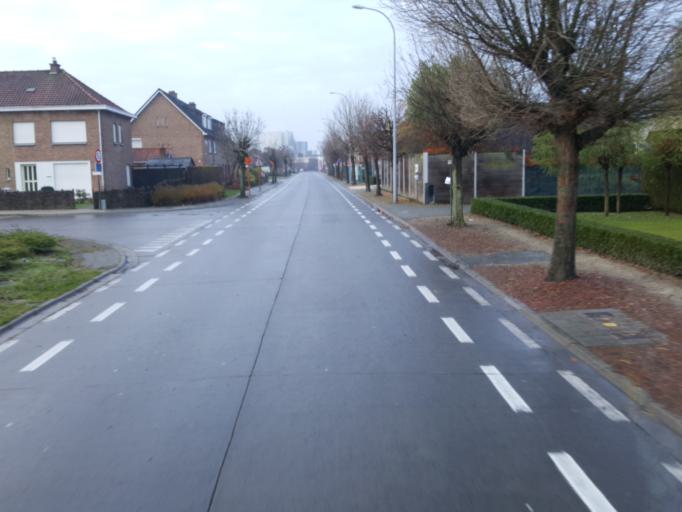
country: BE
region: Flanders
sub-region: Provincie West-Vlaanderen
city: Harelbeke
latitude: 50.8326
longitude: 3.3059
